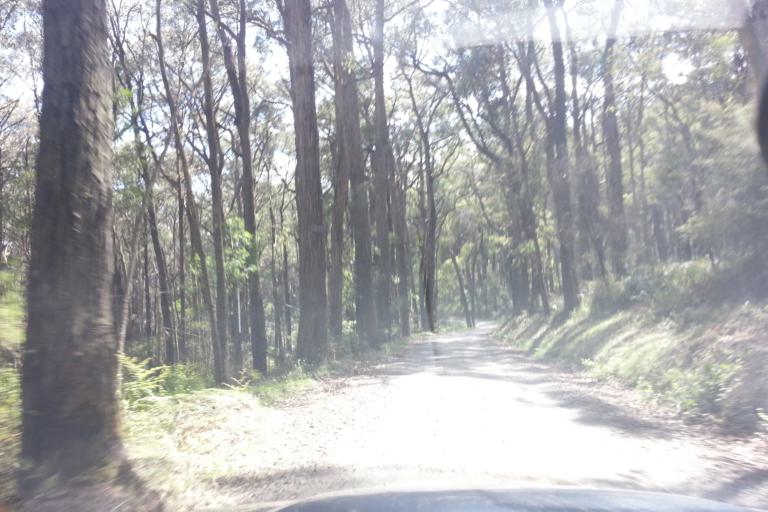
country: AU
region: Victoria
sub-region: Cardinia
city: Gembrook
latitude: -37.9485
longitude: 145.5797
